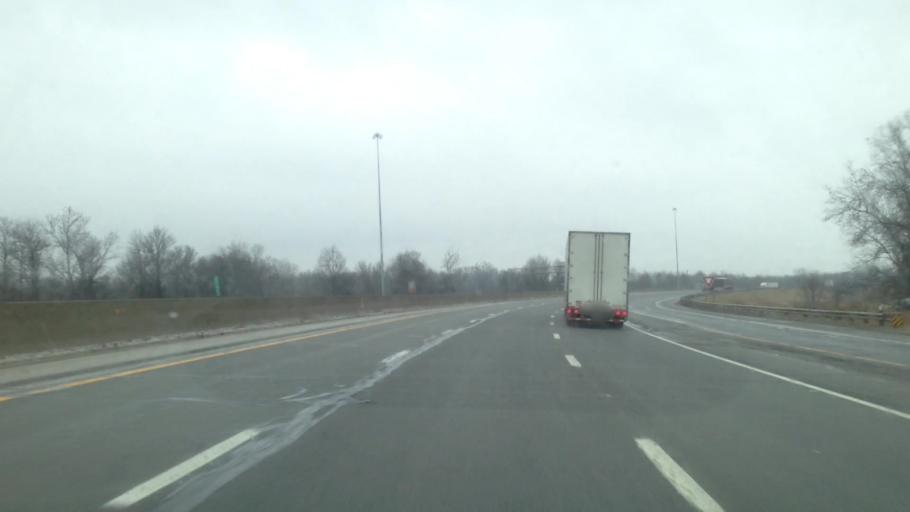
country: US
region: Ohio
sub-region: Trumbull County
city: Newton Falls
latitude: 41.2173
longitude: -80.9529
